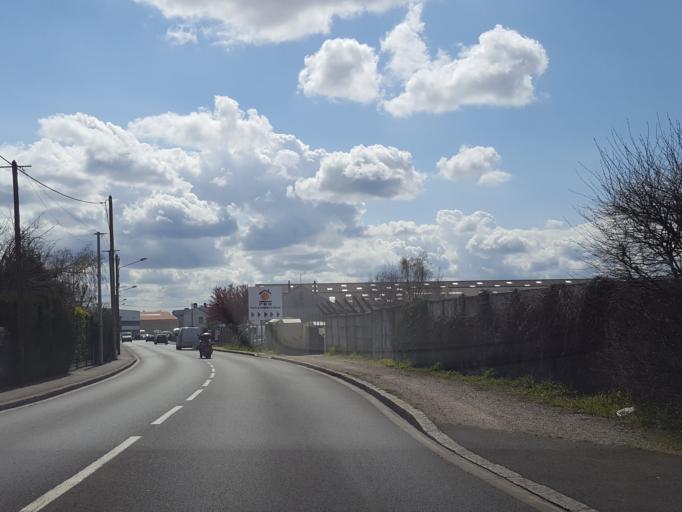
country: FR
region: Centre
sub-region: Departement du Loiret
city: Saint-Jean-de-la-Ruelle
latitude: 47.9099
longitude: 1.8643
